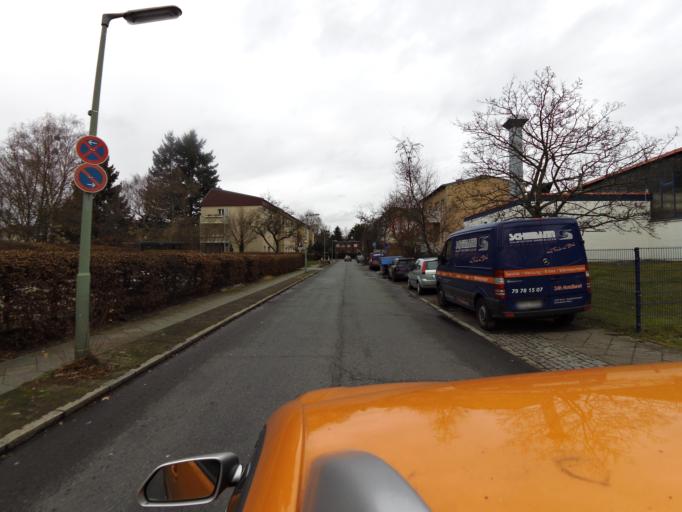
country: DE
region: Berlin
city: Marienfelde
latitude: 52.4353
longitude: 13.3641
